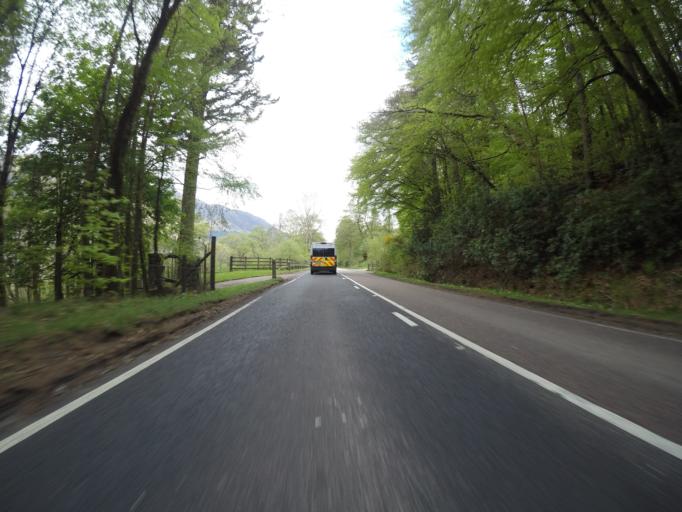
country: GB
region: Scotland
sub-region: Highland
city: Spean Bridge
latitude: 56.9690
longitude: -4.8898
